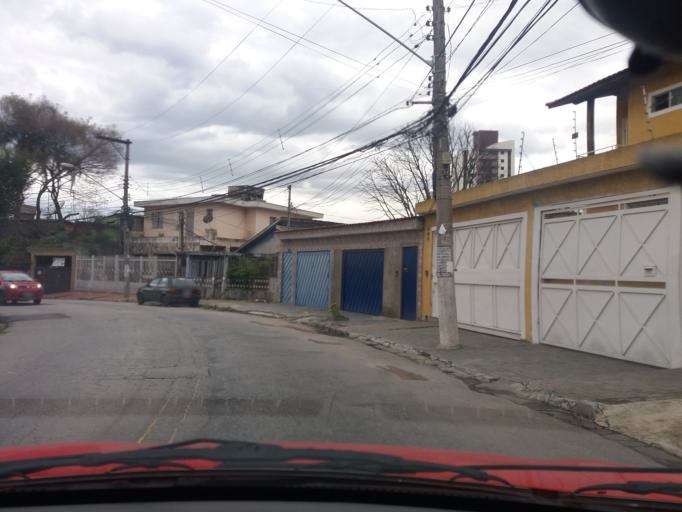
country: BR
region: Sao Paulo
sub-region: Taboao Da Serra
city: Taboao da Serra
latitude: -23.5836
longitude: -46.7392
